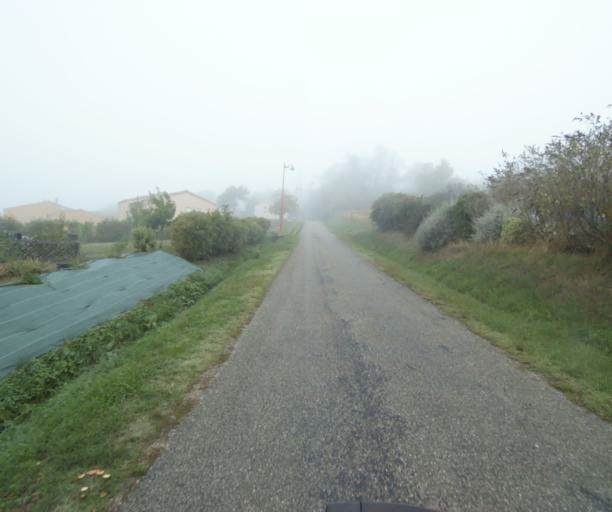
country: FR
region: Midi-Pyrenees
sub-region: Departement du Tarn-et-Garonne
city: Nohic
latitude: 43.9198
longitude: 1.4745
